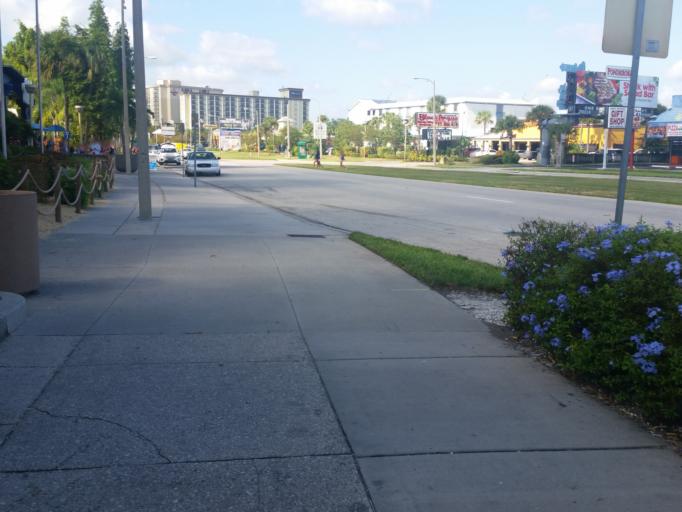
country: US
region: Florida
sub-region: Orange County
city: Tangelo Park
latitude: 28.4620
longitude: -81.4652
